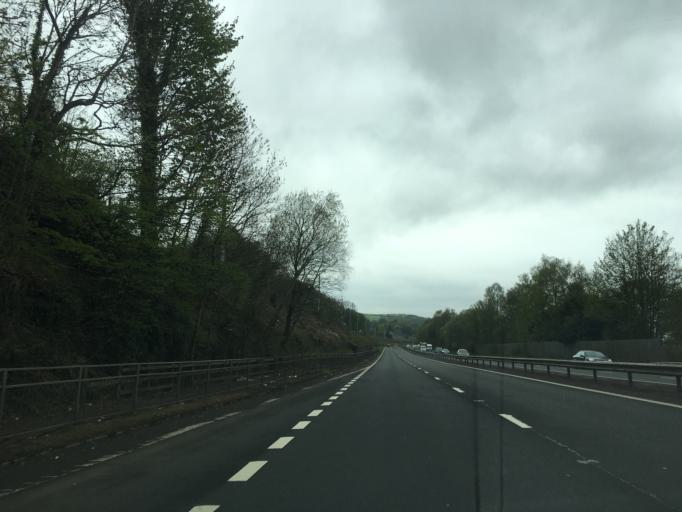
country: GB
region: Scotland
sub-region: West Dunbartonshire
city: Dumbarton
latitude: 55.9232
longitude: -4.5628
